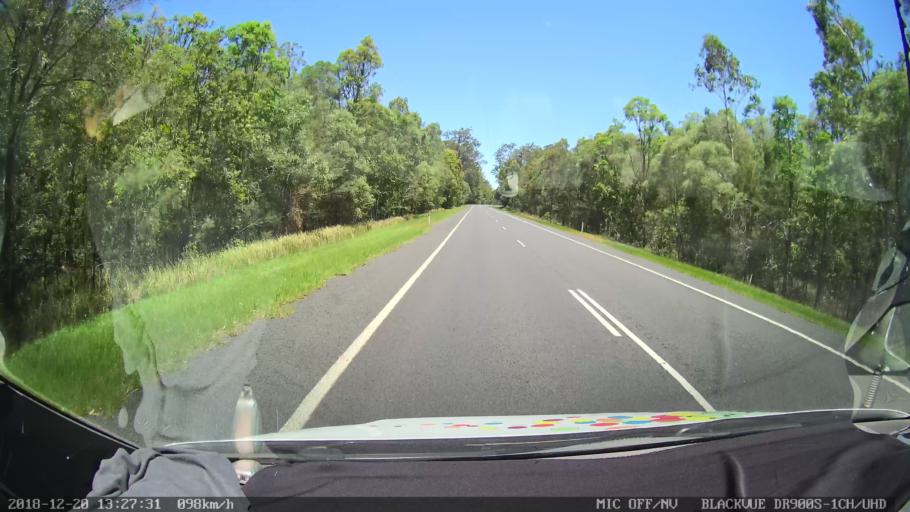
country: AU
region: New South Wales
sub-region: Richmond Valley
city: Casino
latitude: -29.1613
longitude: 152.9922
